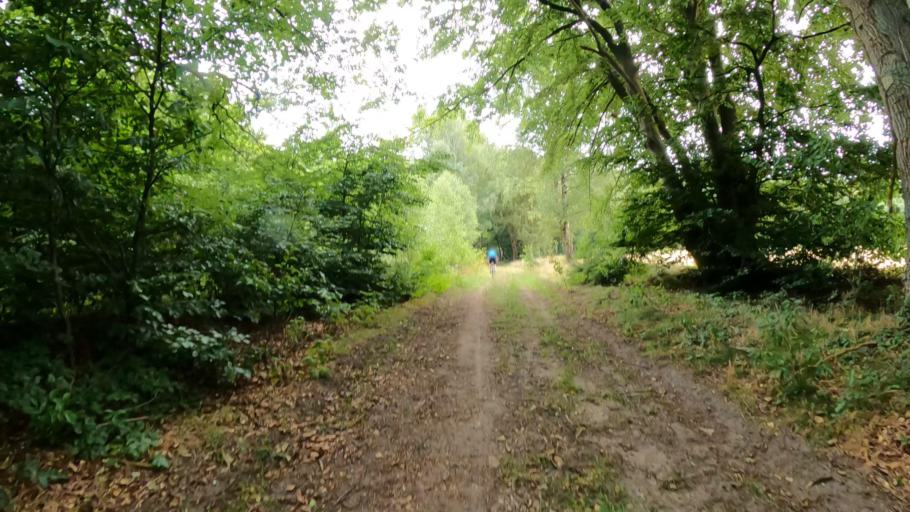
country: DE
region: Schleswig-Holstein
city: Heidmuhlen
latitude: 53.9585
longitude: 10.1007
